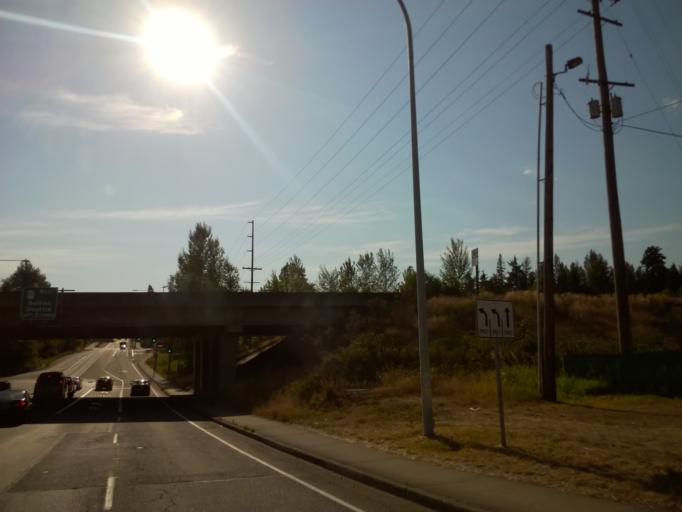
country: US
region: Washington
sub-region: King County
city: Woodinville
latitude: 47.7689
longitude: -122.1570
